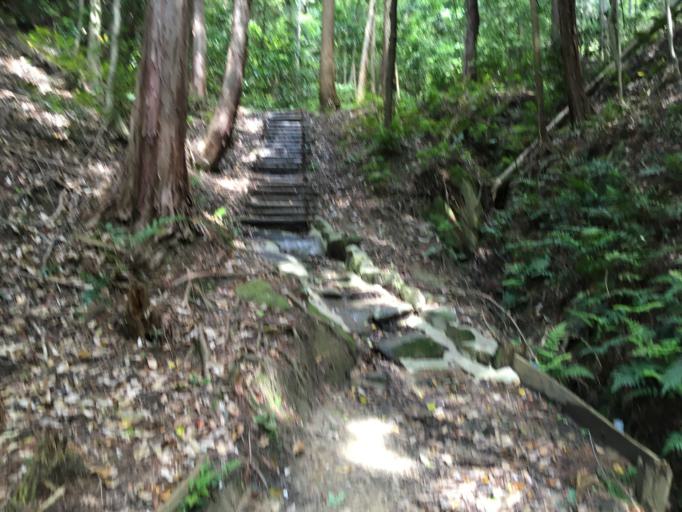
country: JP
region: Nara
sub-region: Ikoma-shi
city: Ikoma
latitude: 34.7059
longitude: 135.7123
